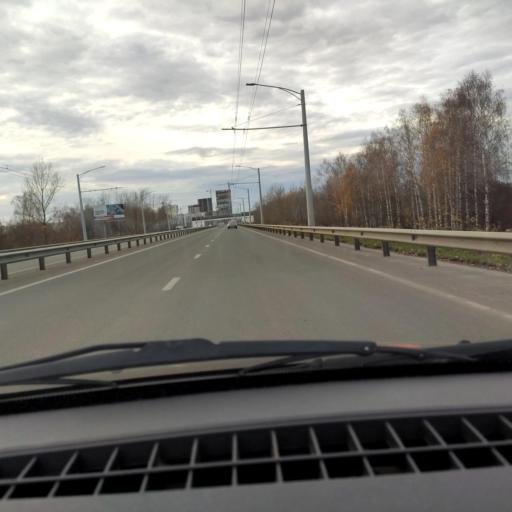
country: RU
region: Bashkortostan
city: Mikhaylovka
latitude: 54.7675
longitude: 55.9234
